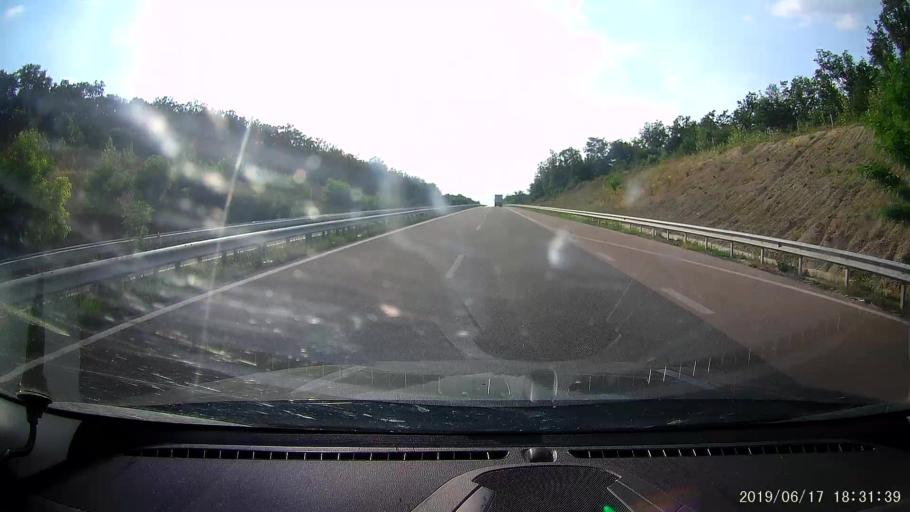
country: BG
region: Khaskovo
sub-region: Obshtina Dimitrovgrad
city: Dimitrovgrad
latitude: 42.0492
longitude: 25.4987
